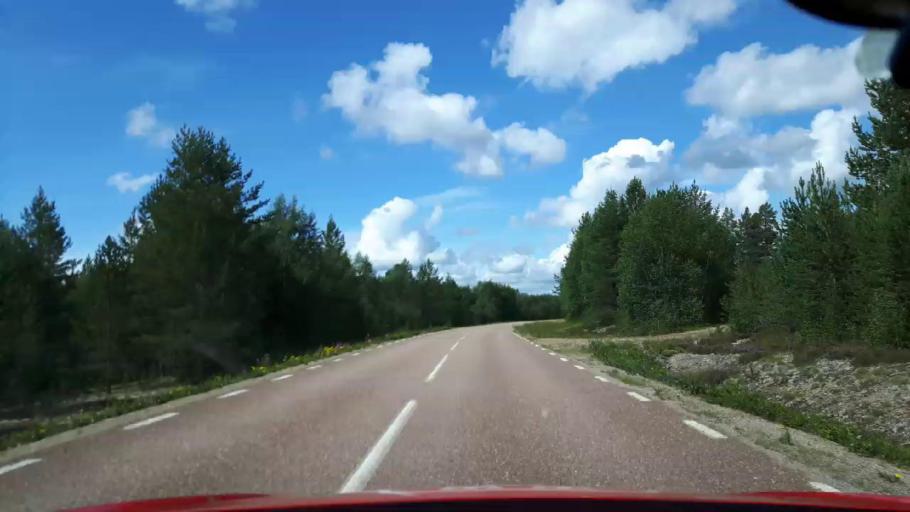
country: SE
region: Dalarna
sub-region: Alvdalens Kommun
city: AElvdalen
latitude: 61.7994
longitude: 13.6732
